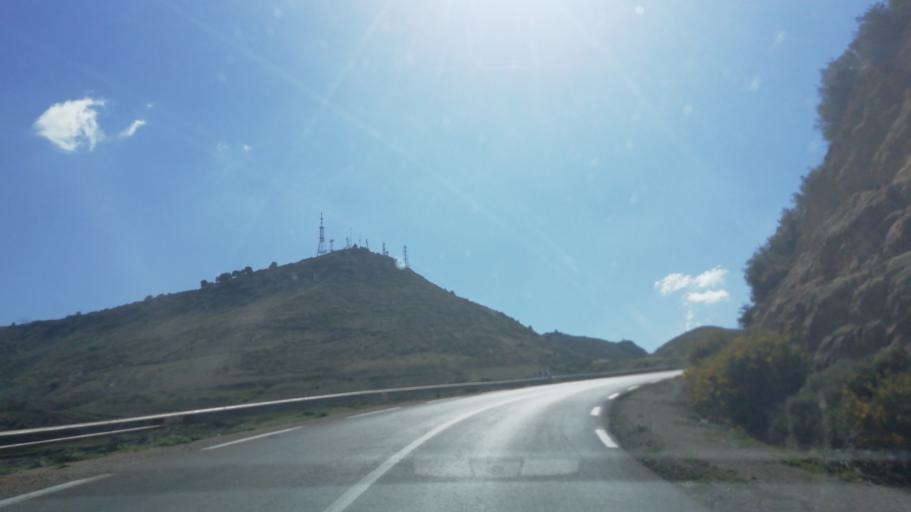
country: DZ
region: Mascara
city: Mascara
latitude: 35.4809
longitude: 0.1598
